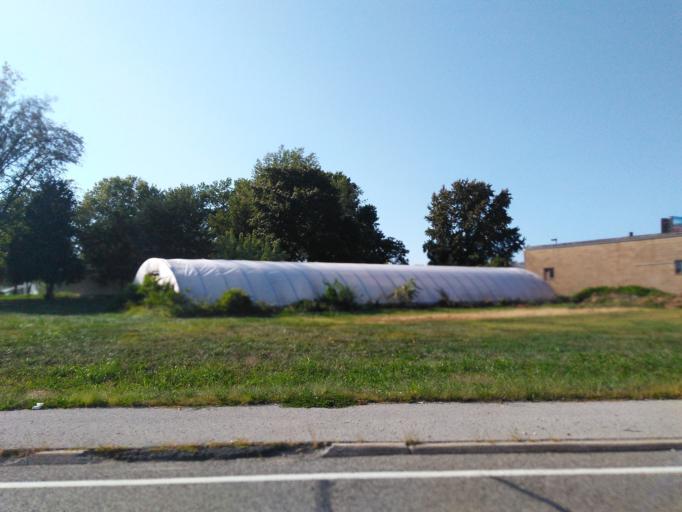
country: US
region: Missouri
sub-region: Saint Louis County
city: Concord
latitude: 38.5226
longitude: -90.3554
